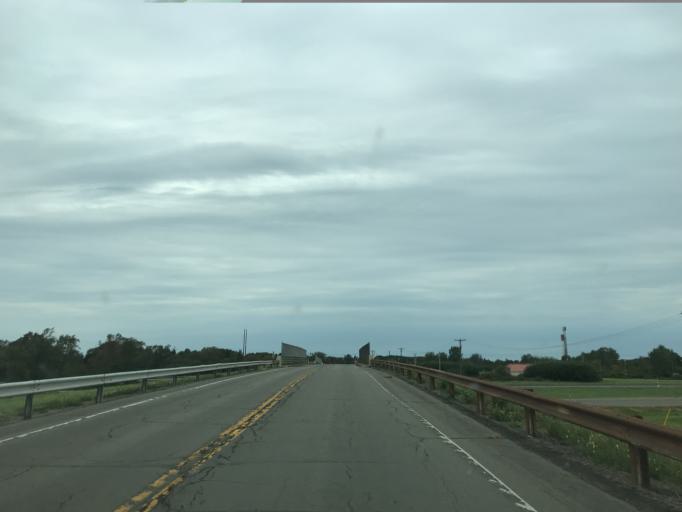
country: US
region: Pennsylvania
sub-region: Erie County
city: North East
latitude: 42.2608
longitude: -79.7442
